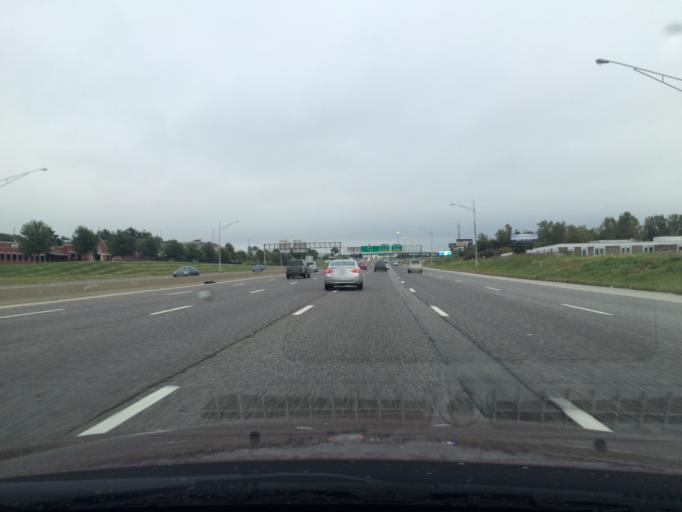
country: US
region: Missouri
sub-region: Saint Charles County
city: Saint Charles
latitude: 38.7539
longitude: -90.4545
